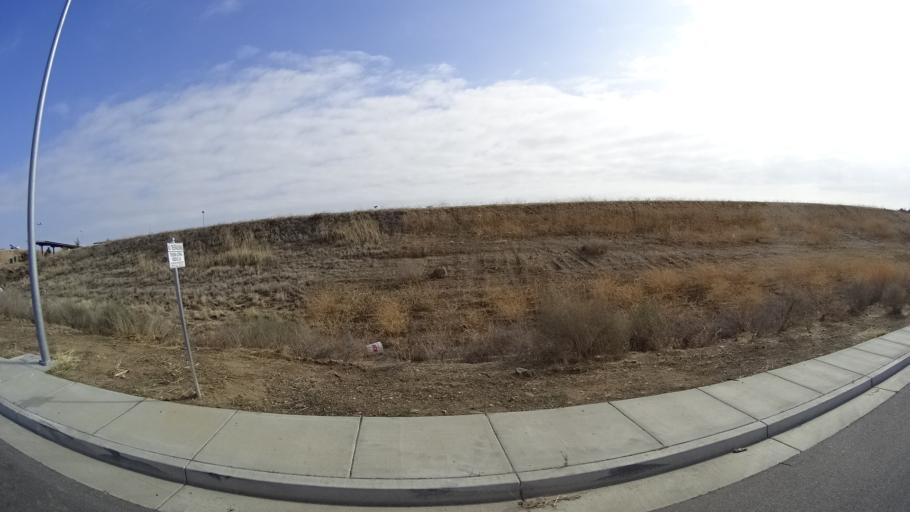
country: US
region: California
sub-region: Kern County
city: Bakersfield
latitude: 35.3936
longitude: -118.9193
